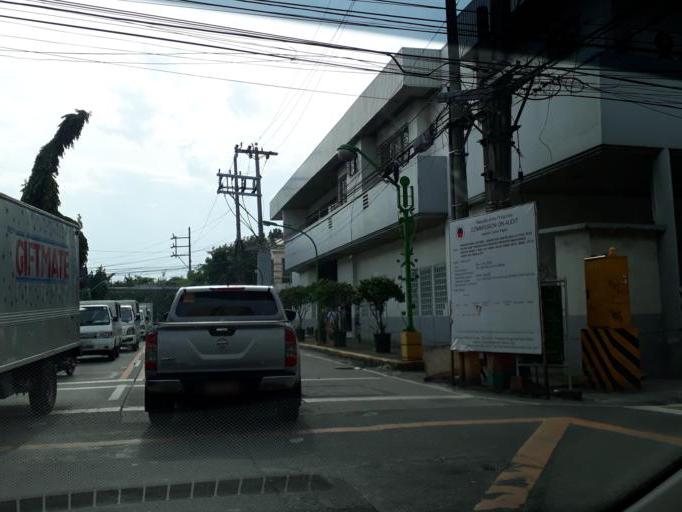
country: PH
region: Metro Manila
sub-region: City of Manila
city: Manila
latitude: 14.6280
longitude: 120.9831
